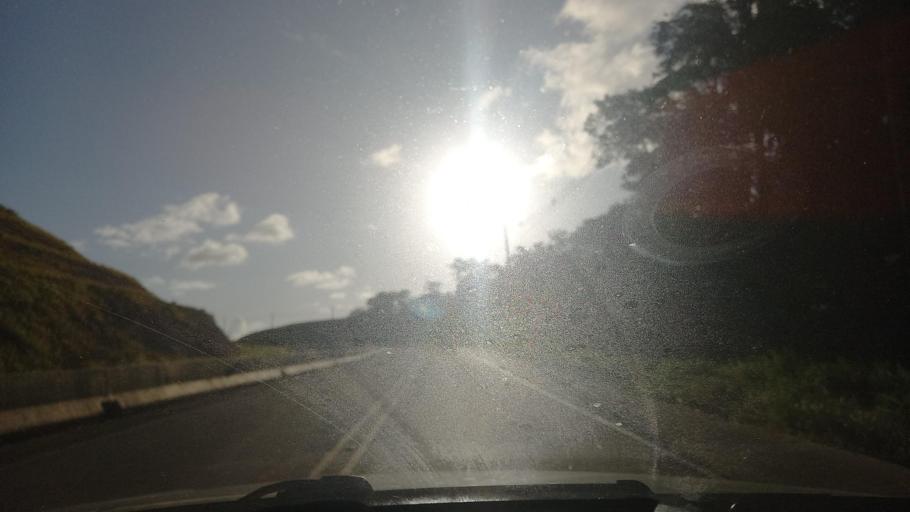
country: BR
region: Alagoas
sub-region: Campo Alegre
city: Campo Alegre
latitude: -9.8220
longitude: -36.2269
